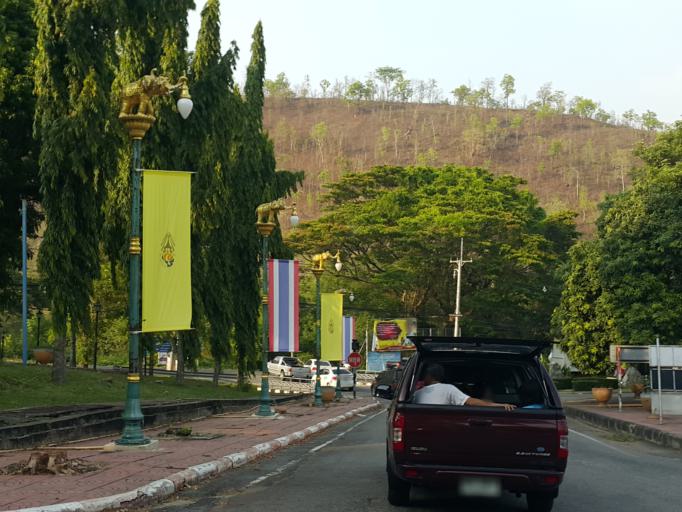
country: TH
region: Kanchanaburi
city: Si Sawat
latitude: 14.3840
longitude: 99.1357
